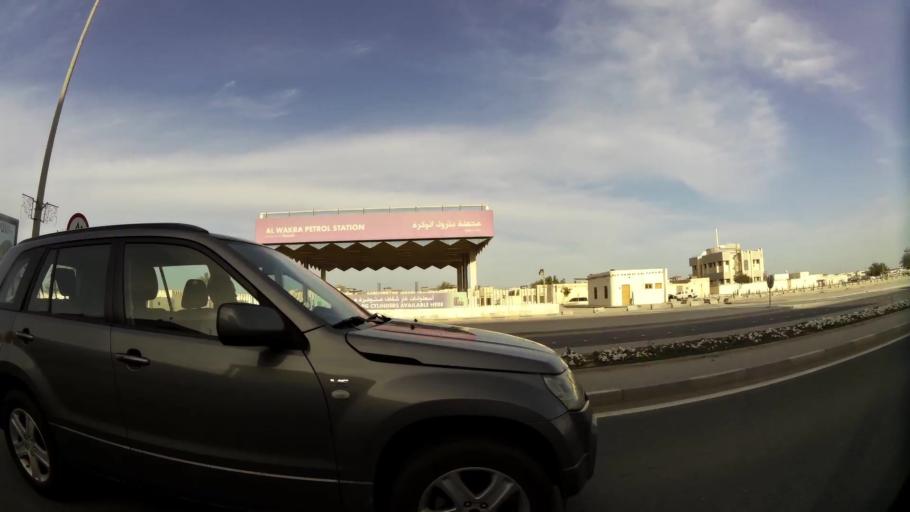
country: QA
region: Al Wakrah
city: Al Wakrah
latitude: 25.1691
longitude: 51.6074
